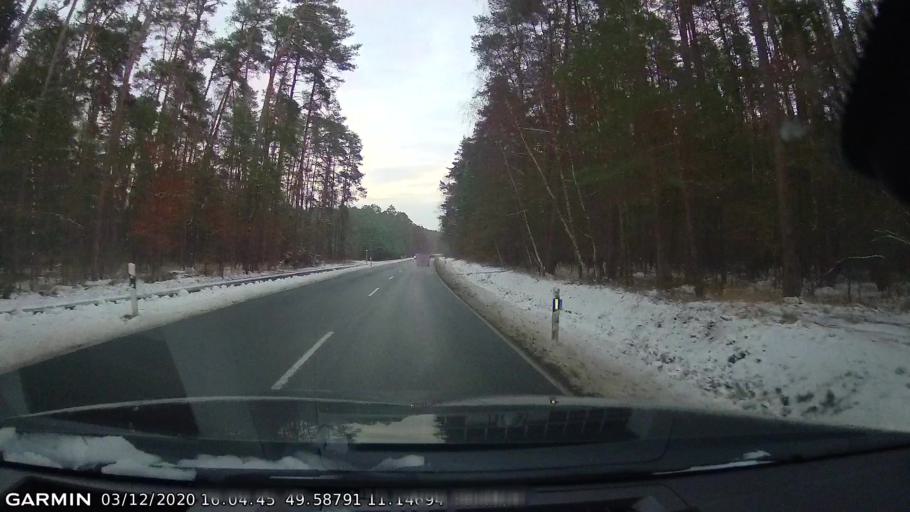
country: DE
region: Bavaria
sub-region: Upper Franconia
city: Kleinsendelbach
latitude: 49.5879
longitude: 11.1472
